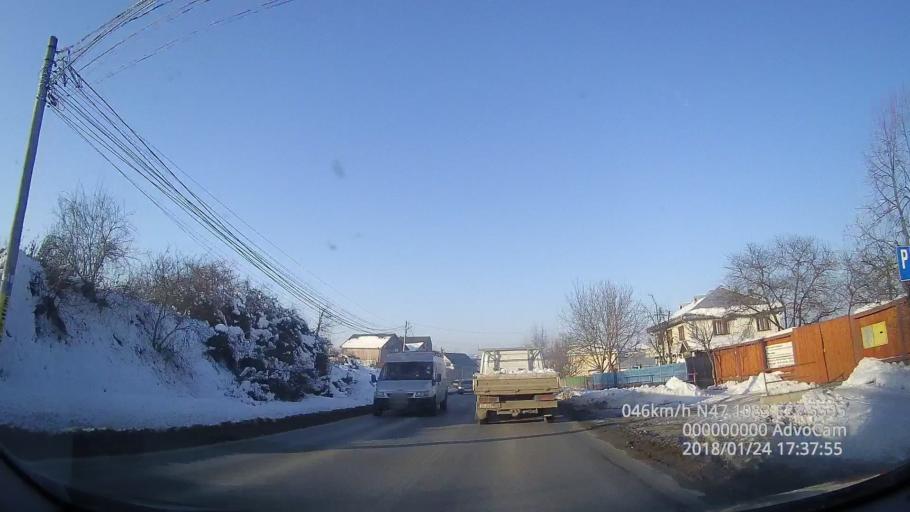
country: RO
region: Iasi
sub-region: Comuna Ciurea
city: Lunca Cetatuii
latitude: 47.1087
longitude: 27.5594
